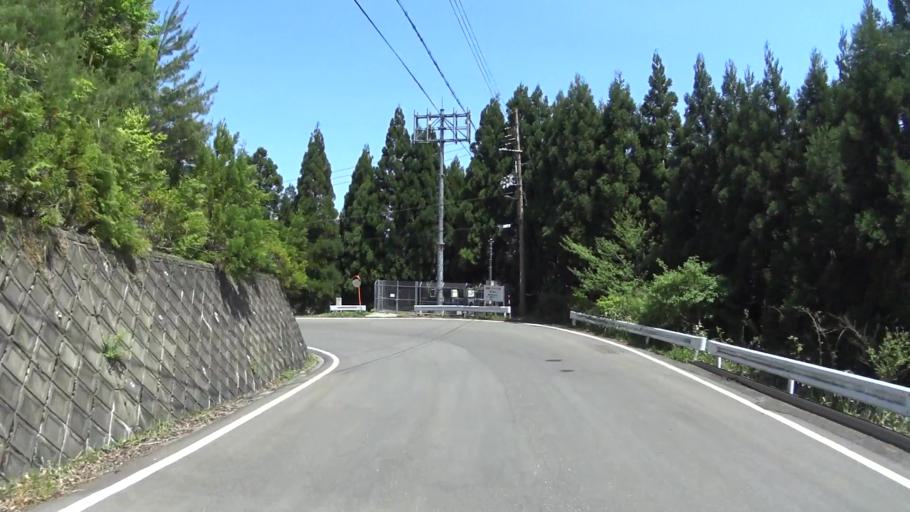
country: JP
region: Kyoto
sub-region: Kyoto-shi
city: Kamigyo-ku
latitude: 35.1603
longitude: 135.7819
